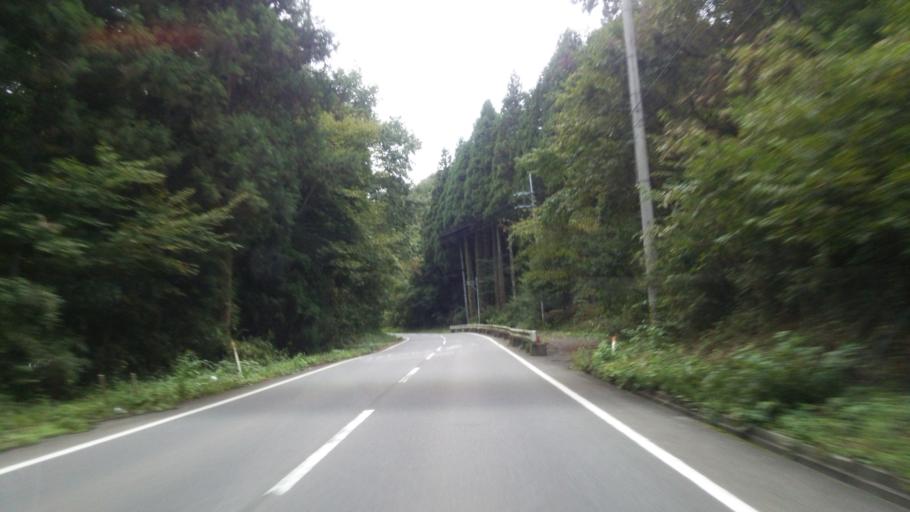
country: JP
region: Fukushima
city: Sukagawa
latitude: 37.2617
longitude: 140.2504
